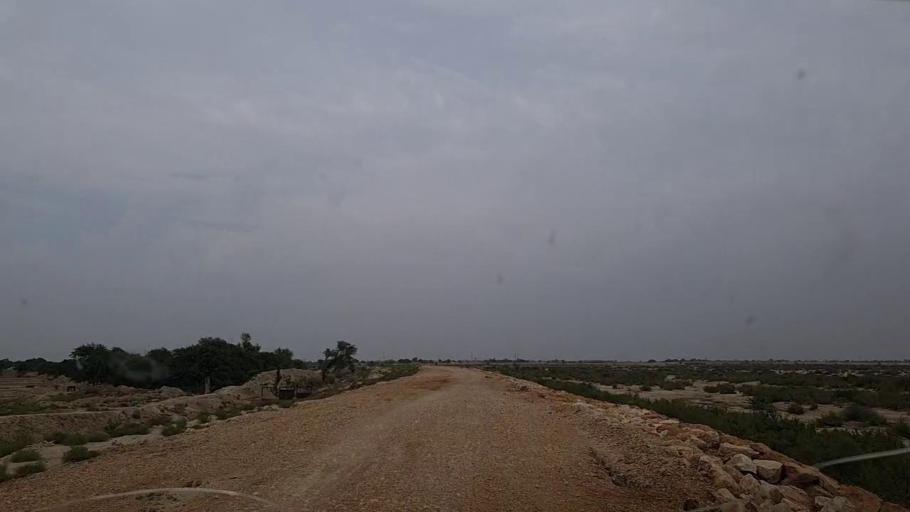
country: PK
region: Sindh
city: Johi
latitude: 26.7069
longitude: 67.5893
